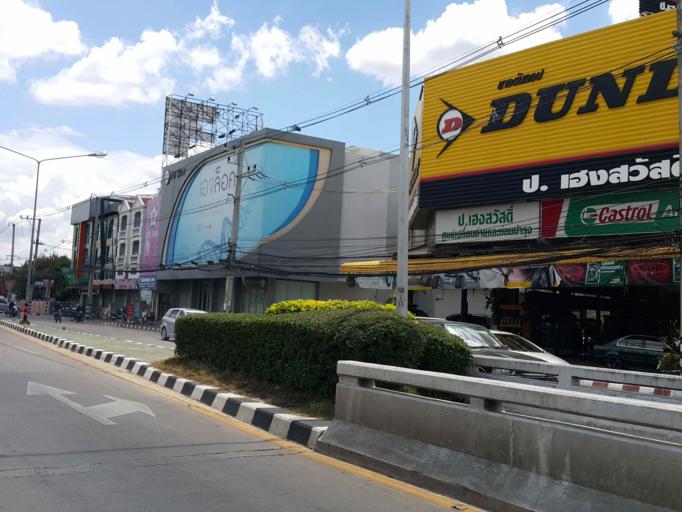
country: TH
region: Chiang Mai
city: Chiang Mai
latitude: 18.7626
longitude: 98.9730
